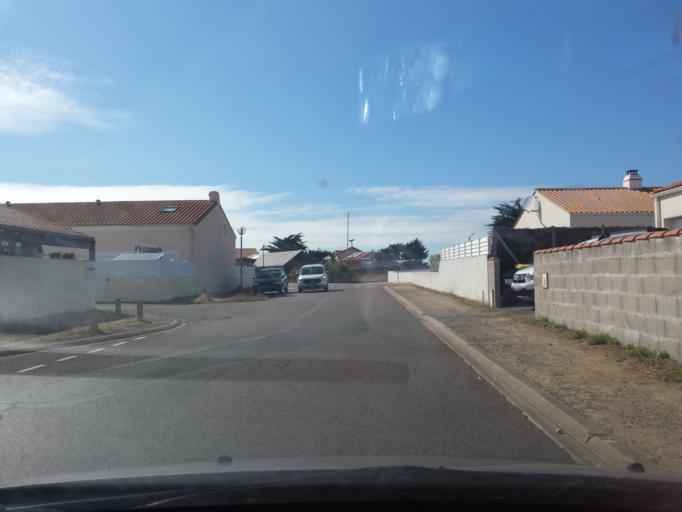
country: FR
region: Pays de la Loire
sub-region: Departement de la Vendee
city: Bretignolles-sur-Mer
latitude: 46.6173
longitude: -1.8614
